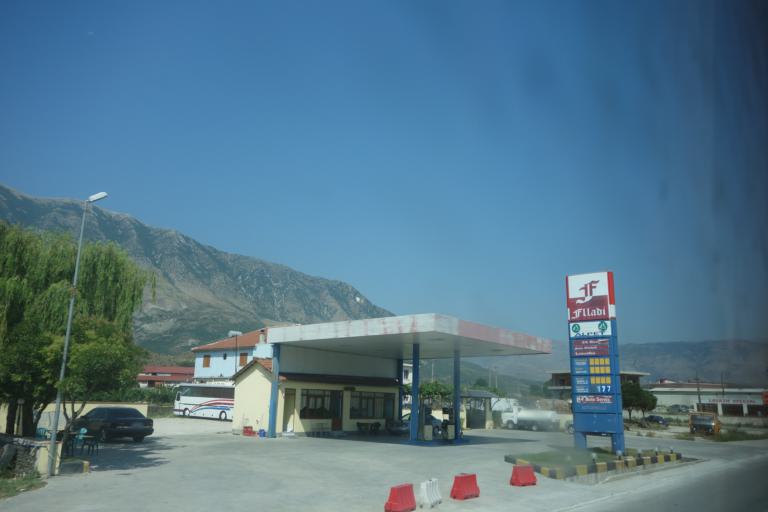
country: AL
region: Gjirokaster
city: Gjirokaster
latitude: 40.1228
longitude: 20.1131
